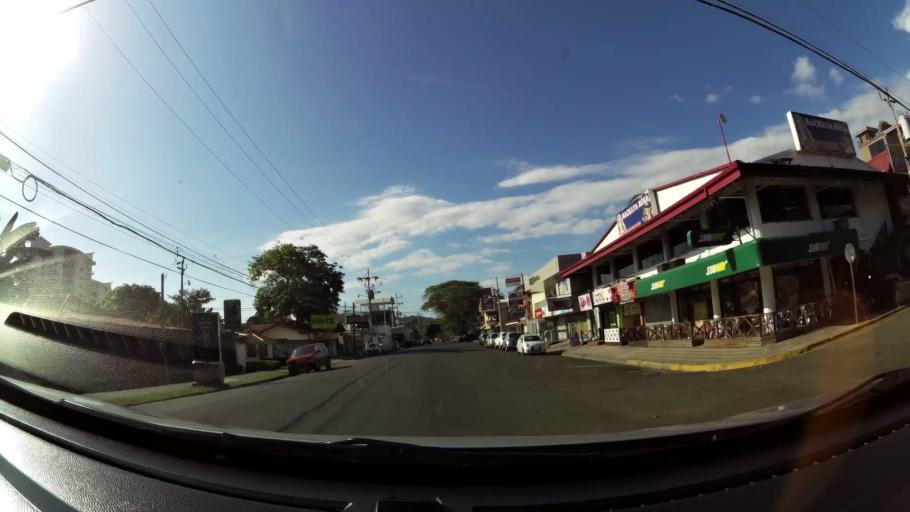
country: CR
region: Puntarenas
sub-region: Canton de Garabito
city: Jaco
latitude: 9.6164
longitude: -84.6301
